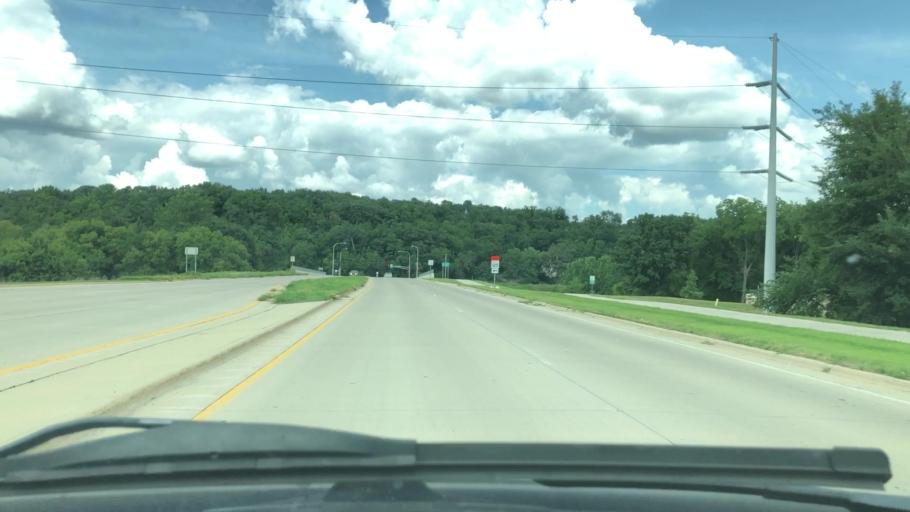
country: US
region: Minnesota
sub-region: Olmsted County
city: Rochester
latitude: 43.9959
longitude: -92.4983
